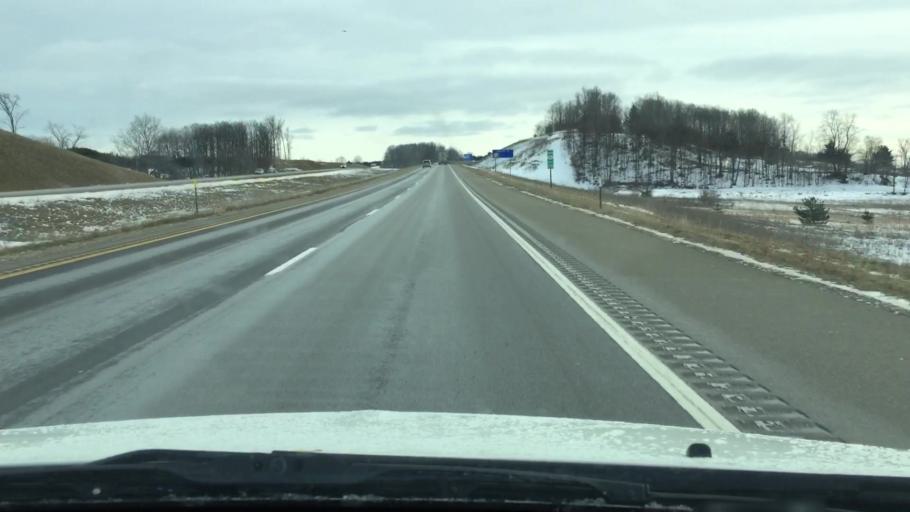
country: US
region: Michigan
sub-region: Wexford County
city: Manton
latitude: 44.4239
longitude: -85.3854
